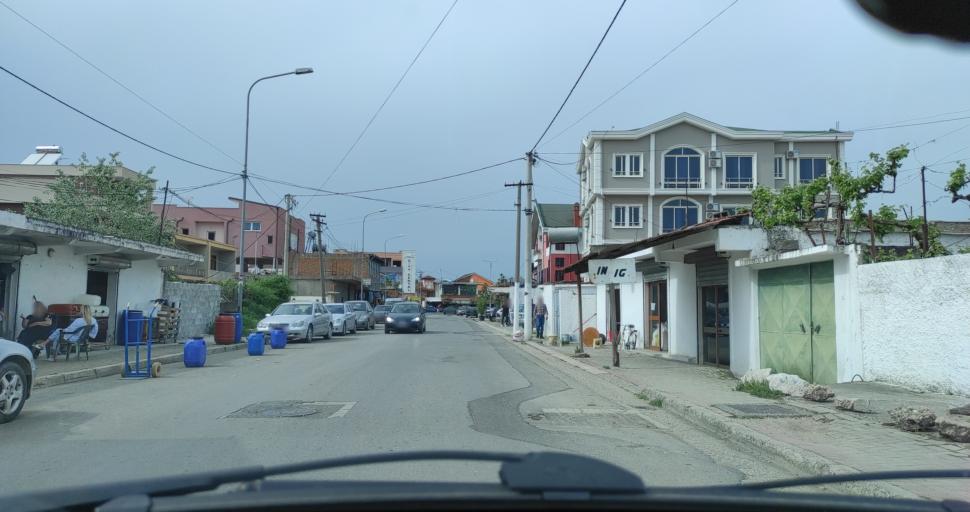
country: AL
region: Durres
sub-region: Rrethi i Krujes
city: Fushe-Kruje
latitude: 41.4776
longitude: 19.7177
